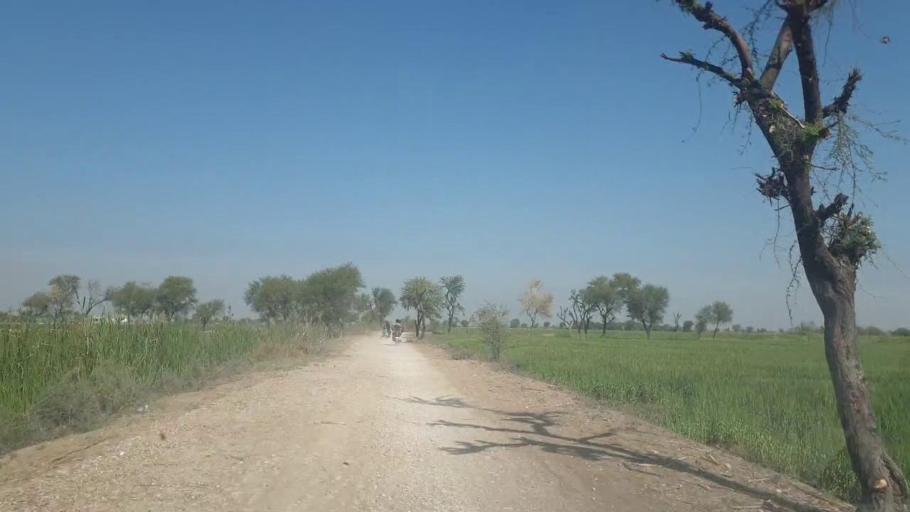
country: PK
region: Sindh
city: Mirpur Khas
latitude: 25.5530
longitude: 69.1966
